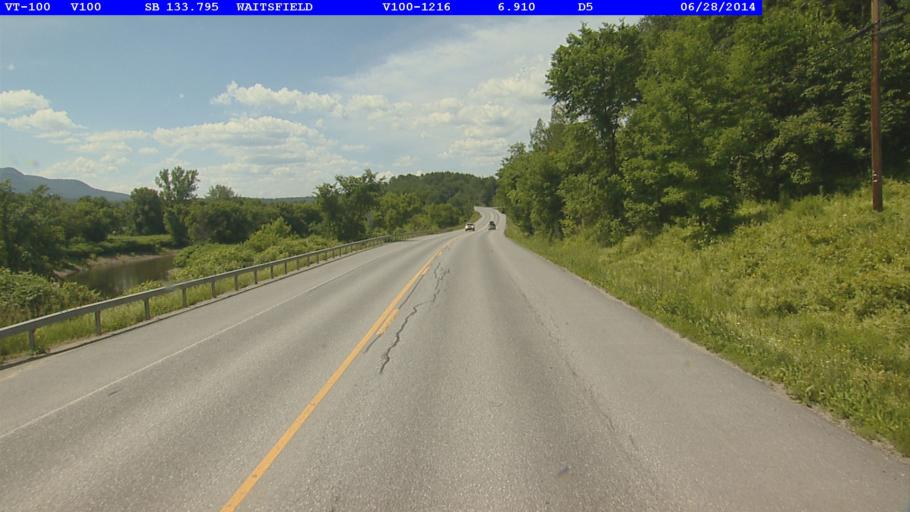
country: US
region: Vermont
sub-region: Washington County
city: Waterbury
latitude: 44.2265
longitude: -72.7863
